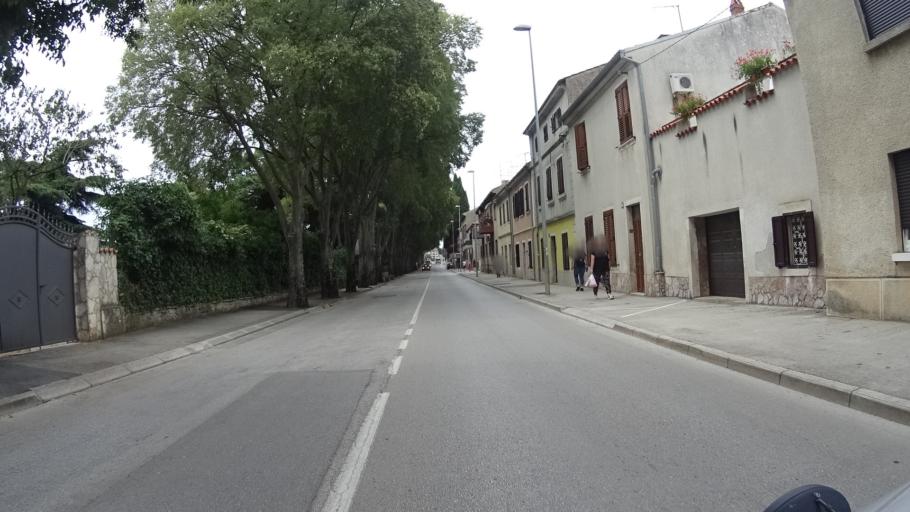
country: HR
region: Istarska
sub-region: Grad Pula
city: Pula
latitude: 44.8638
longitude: 13.8560
